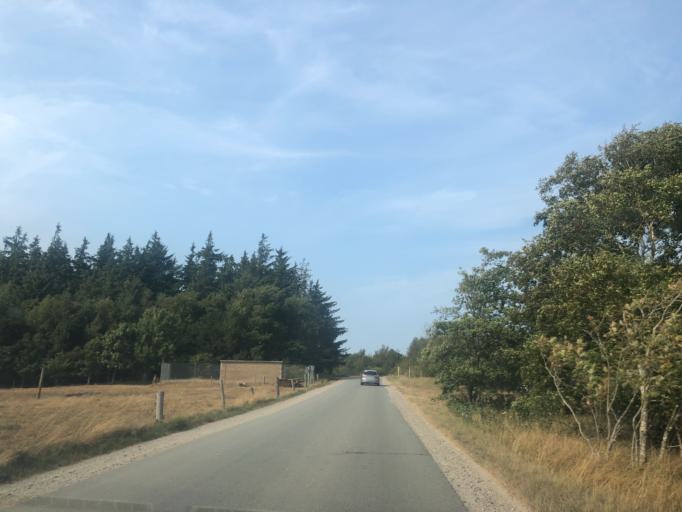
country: DK
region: North Denmark
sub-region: Morso Kommune
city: Nykobing Mors
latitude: 56.8354
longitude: 9.0455
